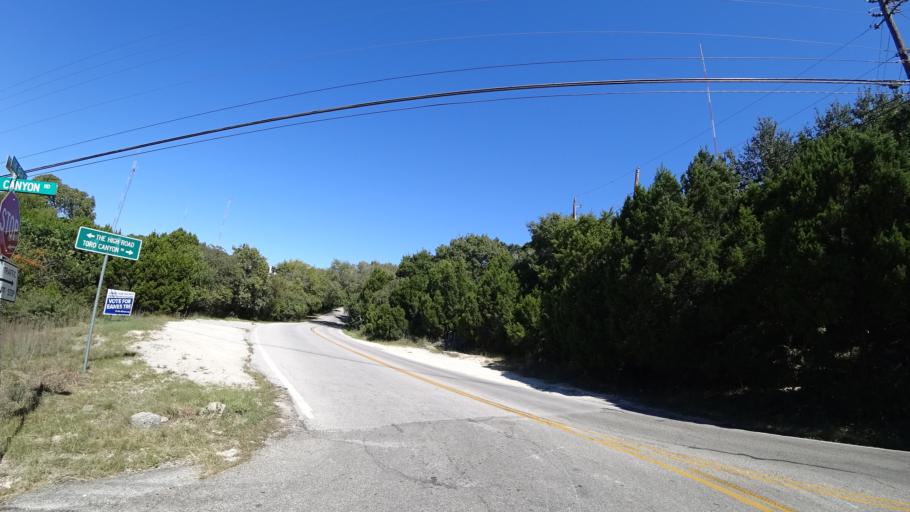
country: US
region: Texas
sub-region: Travis County
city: West Lake Hills
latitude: 30.3084
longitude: -97.7973
